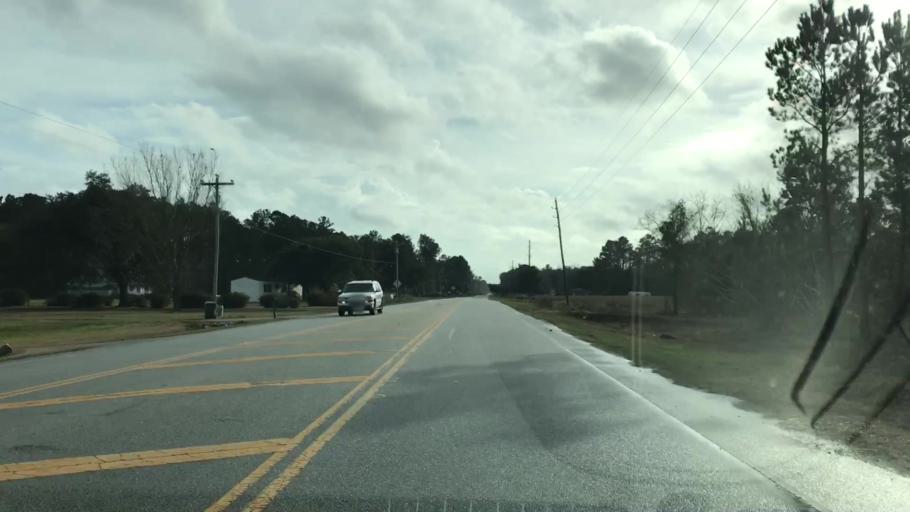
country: US
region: South Carolina
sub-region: Williamsburg County
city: Andrews
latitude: 33.4412
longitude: -79.5913
